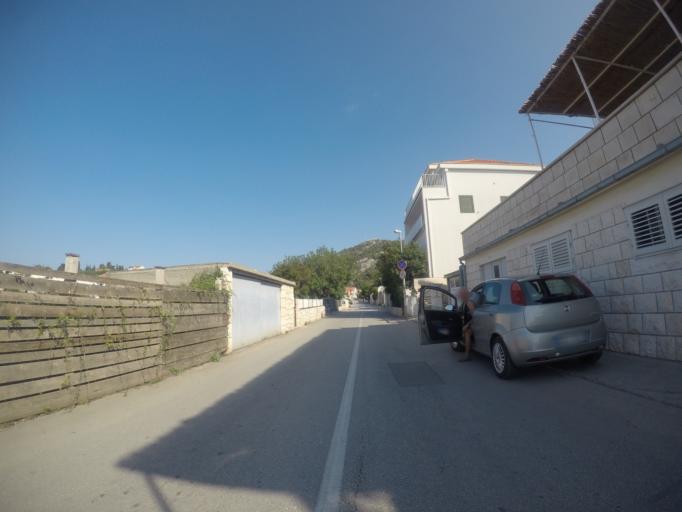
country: HR
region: Splitsko-Dalmatinska
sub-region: Grad Hvar
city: Hvar
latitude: 43.1686
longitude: 16.4460
